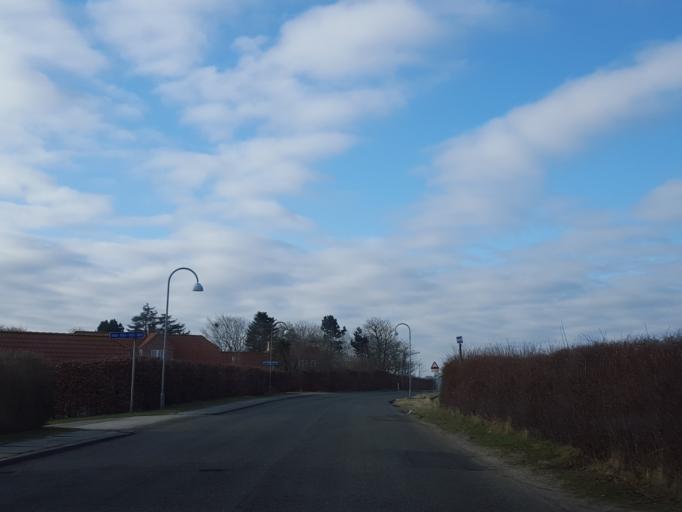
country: DK
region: North Denmark
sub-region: Alborg Kommune
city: Gistrup
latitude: 57.0085
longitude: 9.9785
